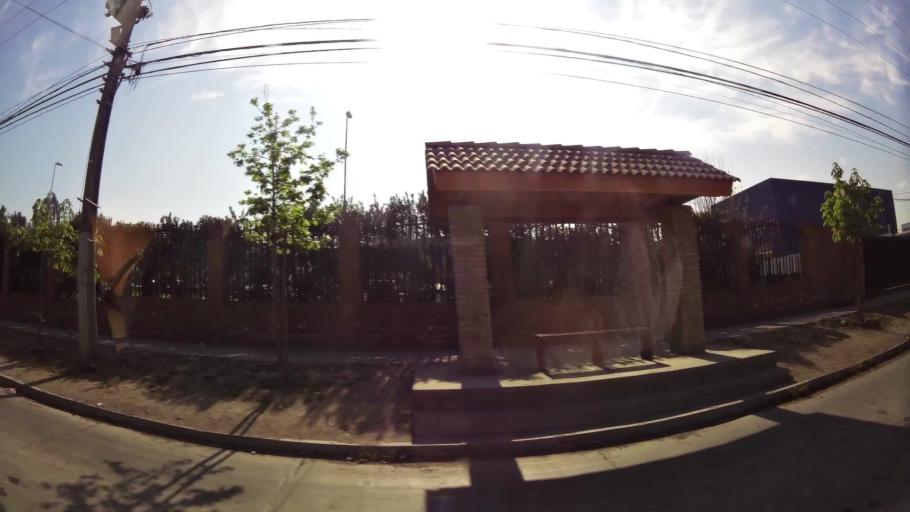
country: CL
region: Santiago Metropolitan
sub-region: Provincia de Talagante
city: Penaflor
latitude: -33.5598
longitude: -70.8233
